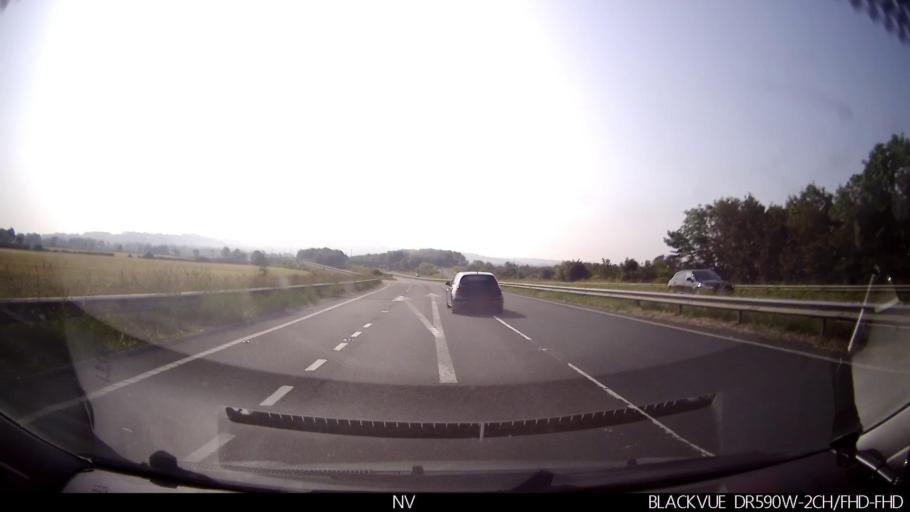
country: GB
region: England
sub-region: North Yorkshire
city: Malton
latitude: 54.1440
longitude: -0.7541
